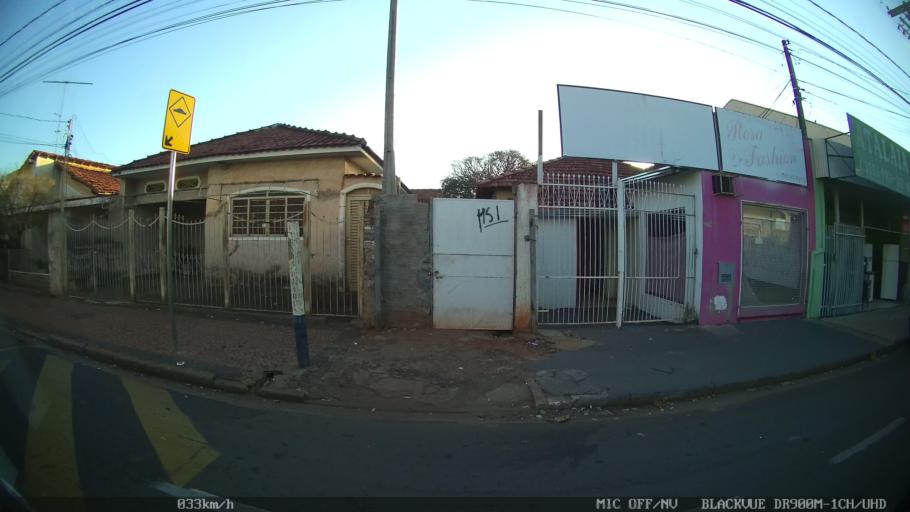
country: BR
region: Sao Paulo
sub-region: Sao Jose Do Rio Preto
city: Sao Jose do Rio Preto
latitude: -20.7937
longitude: -49.3696
